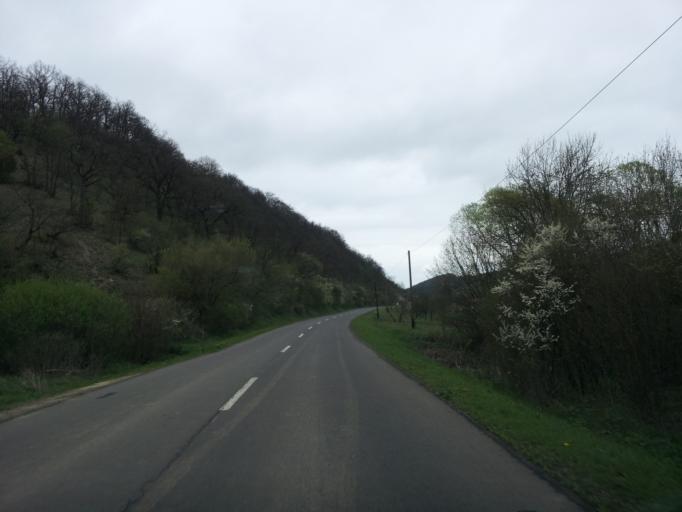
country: HU
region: Borsod-Abauj-Zemplen
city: Rudabanya
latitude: 48.4808
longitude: 20.6130
